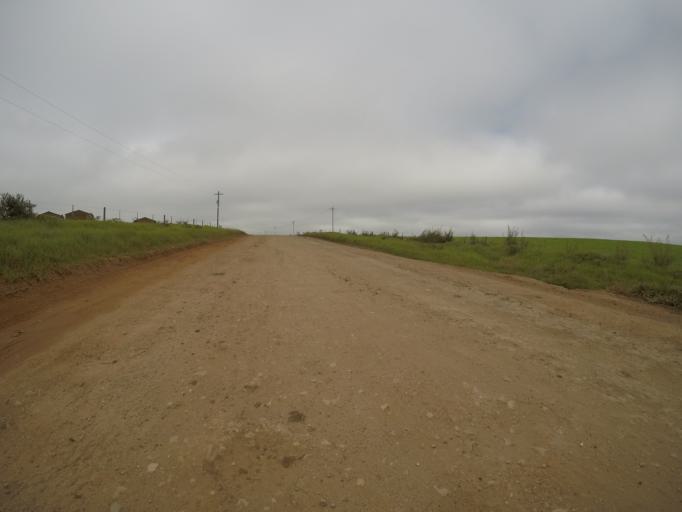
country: ZA
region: Eastern Cape
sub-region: Cacadu District Municipality
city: Kareedouw
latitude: -34.0230
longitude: 24.2406
